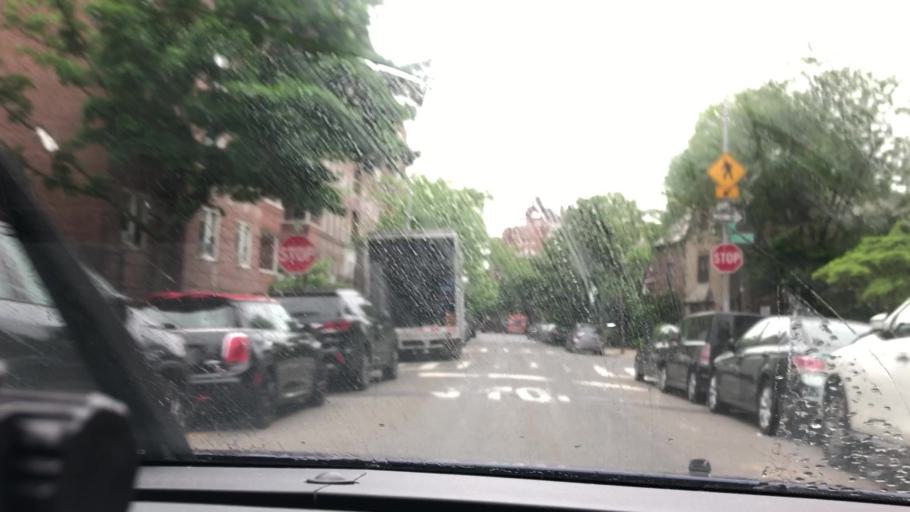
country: US
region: New York
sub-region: Queens County
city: Borough of Queens
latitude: 40.7161
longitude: -73.8370
